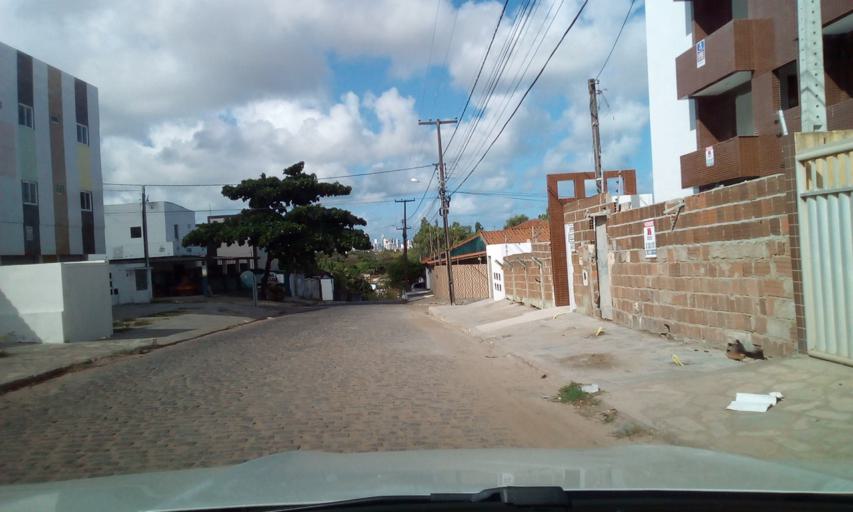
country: BR
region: Paraiba
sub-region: Joao Pessoa
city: Joao Pessoa
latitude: -7.1761
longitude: -34.8505
